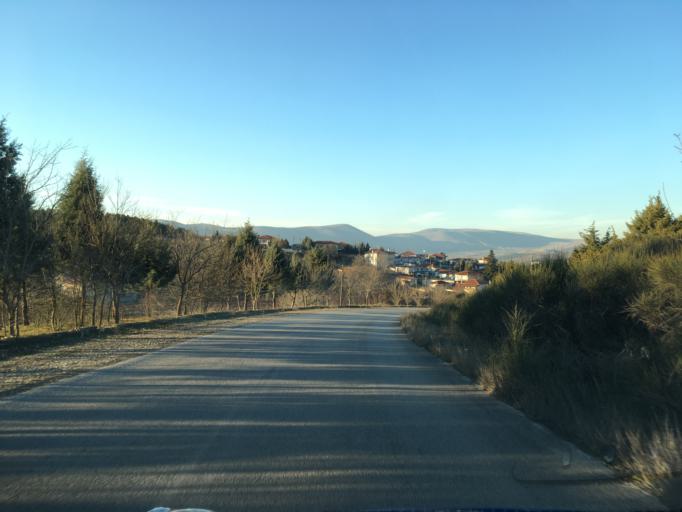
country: GR
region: West Macedonia
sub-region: Nomos Kozanis
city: Kozani
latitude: 40.2820
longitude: 21.7326
